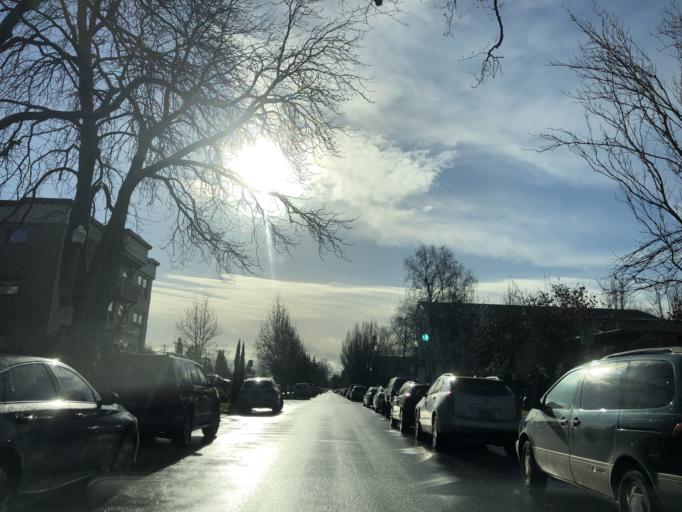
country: US
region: Washington
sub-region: Pierce County
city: Tacoma
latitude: 47.2585
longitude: -122.4561
